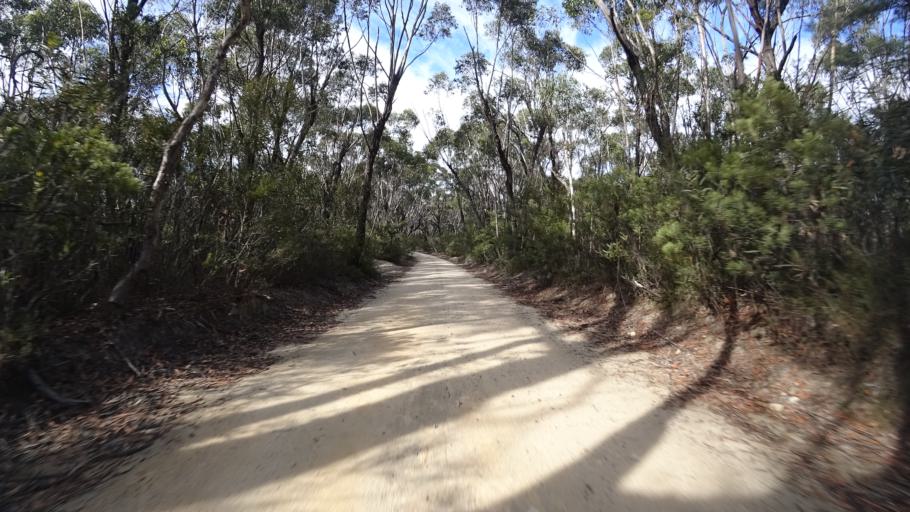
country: AU
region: New South Wales
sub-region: Lithgow
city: Lithgow
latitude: -33.5006
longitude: 150.1629
